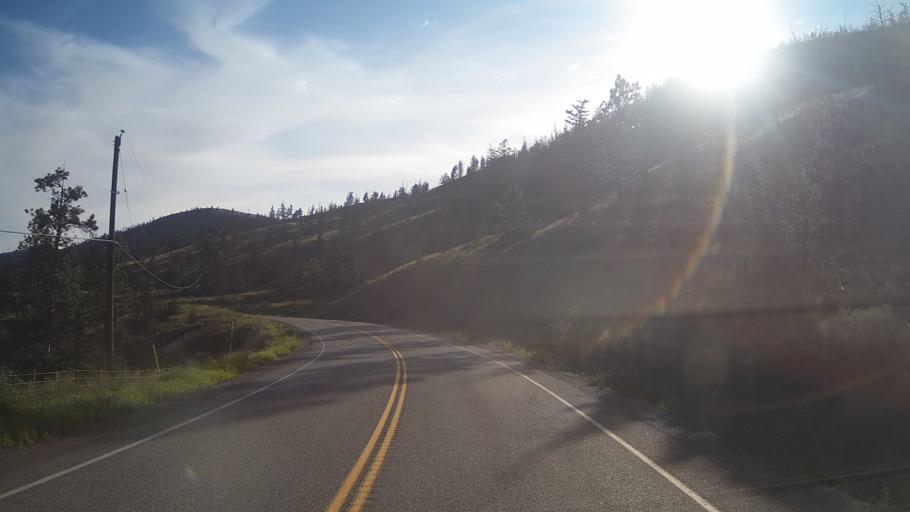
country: CA
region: British Columbia
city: Cache Creek
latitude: 50.8825
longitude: -121.5056
